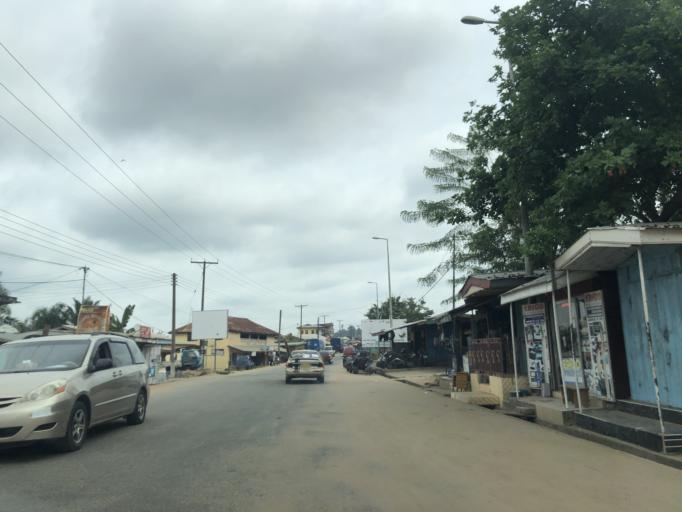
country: GH
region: Eastern
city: Koforidua
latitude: 6.1136
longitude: -0.2702
